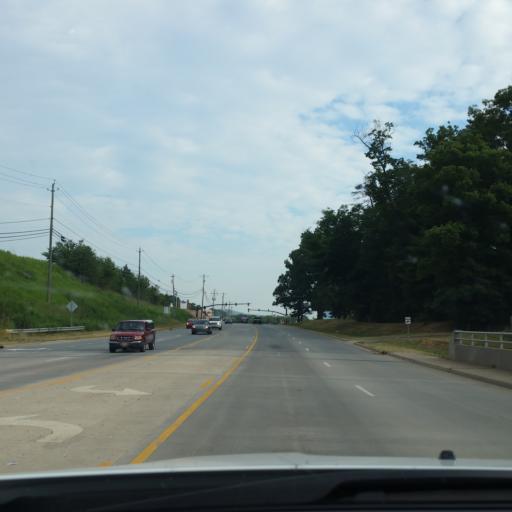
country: US
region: North Carolina
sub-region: Buncombe County
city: Bent Creek
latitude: 35.5412
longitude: -82.6563
